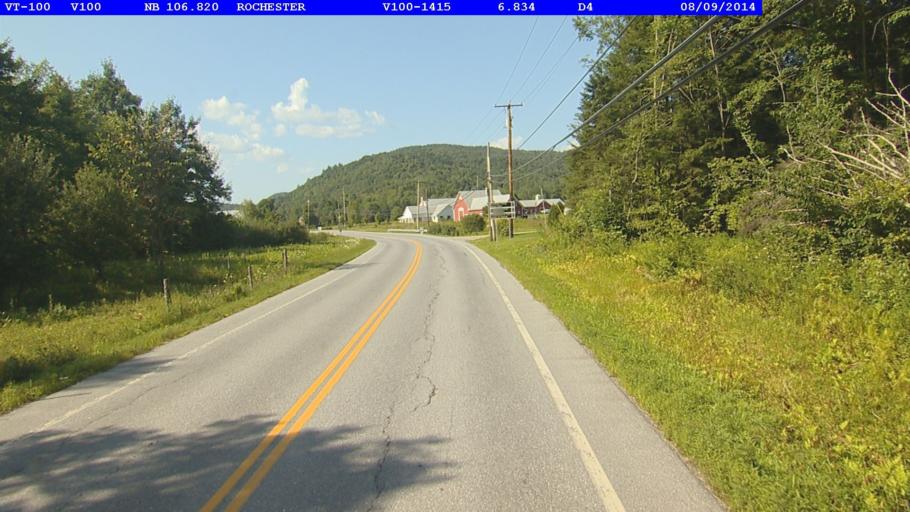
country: US
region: Vermont
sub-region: Orange County
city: Randolph
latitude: 43.8935
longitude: -72.8184
